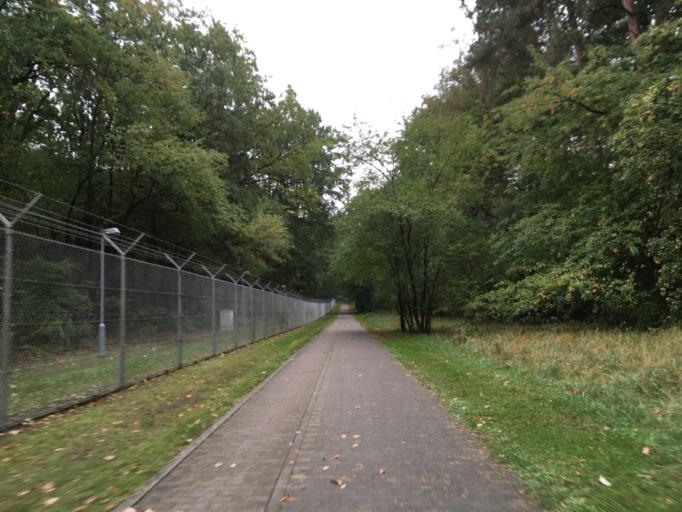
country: DE
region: Brandenburg
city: Ahrensfelde
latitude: 52.5953
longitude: 13.5797
